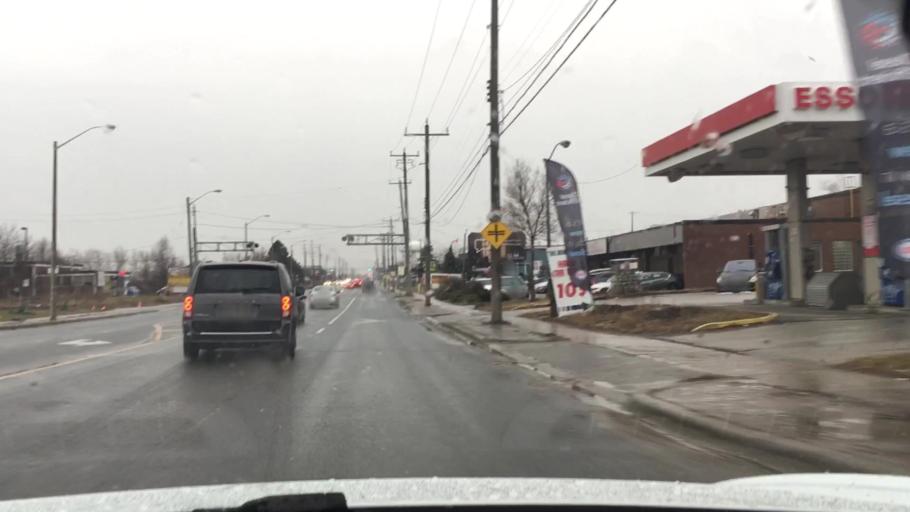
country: CA
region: Ontario
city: Scarborough
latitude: 43.7184
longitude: -79.2836
